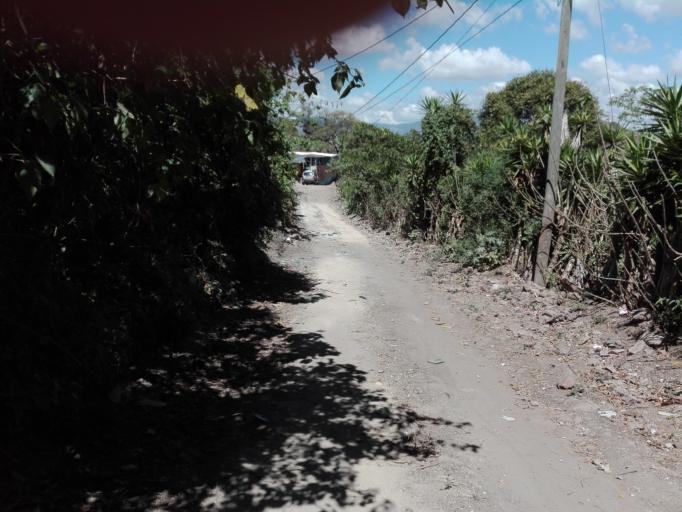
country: GT
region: Guatemala
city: Amatitlan
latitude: 14.4399
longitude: -90.5882
